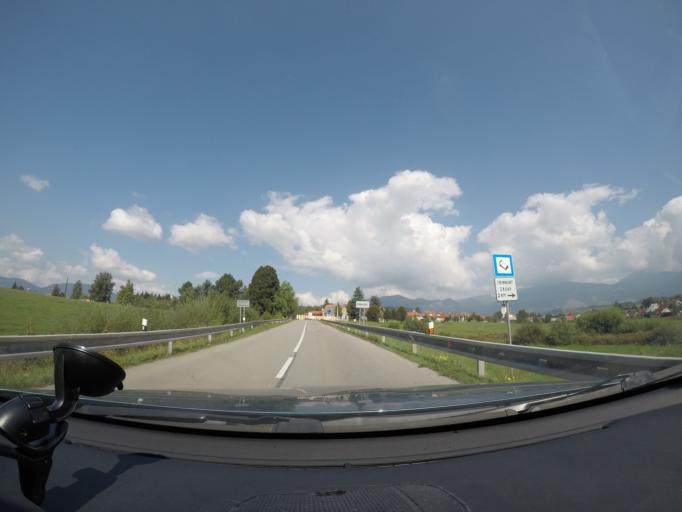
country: SK
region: Zilinsky
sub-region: Okres Liptovsky Mikulas
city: Liptovsky Mikulas
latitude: 49.1135
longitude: 19.6028
